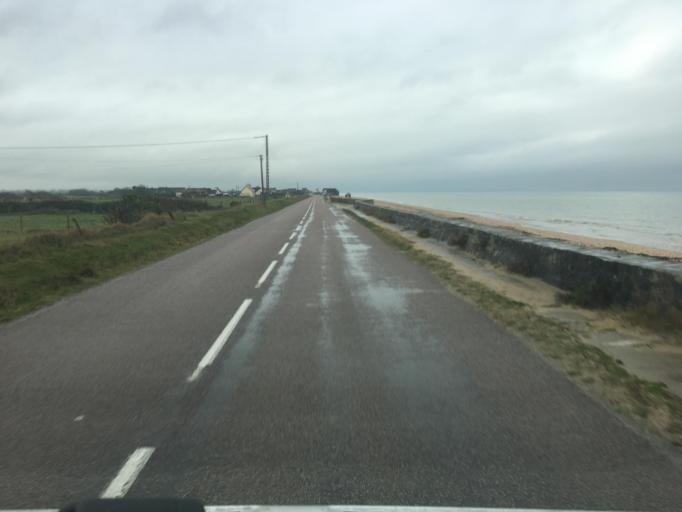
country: FR
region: Lower Normandy
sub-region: Departement de la Manche
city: Sainte-Mere-Eglise
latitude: 49.4595
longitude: -1.2271
